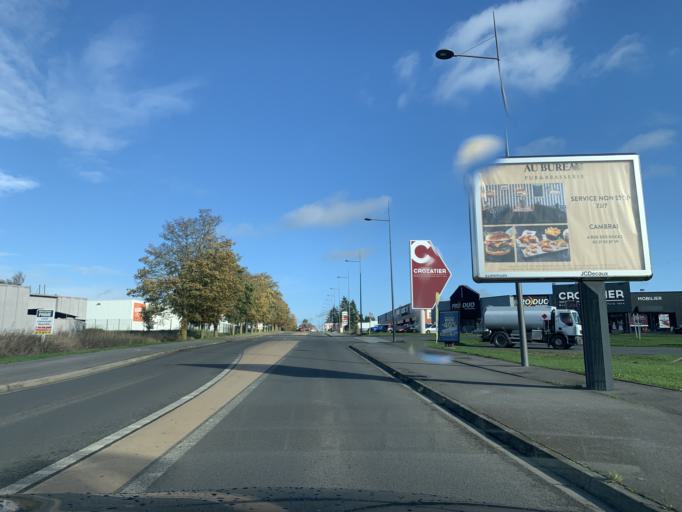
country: FR
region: Nord-Pas-de-Calais
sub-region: Departement du Nord
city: Proville
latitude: 50.1507
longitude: 3.2209
